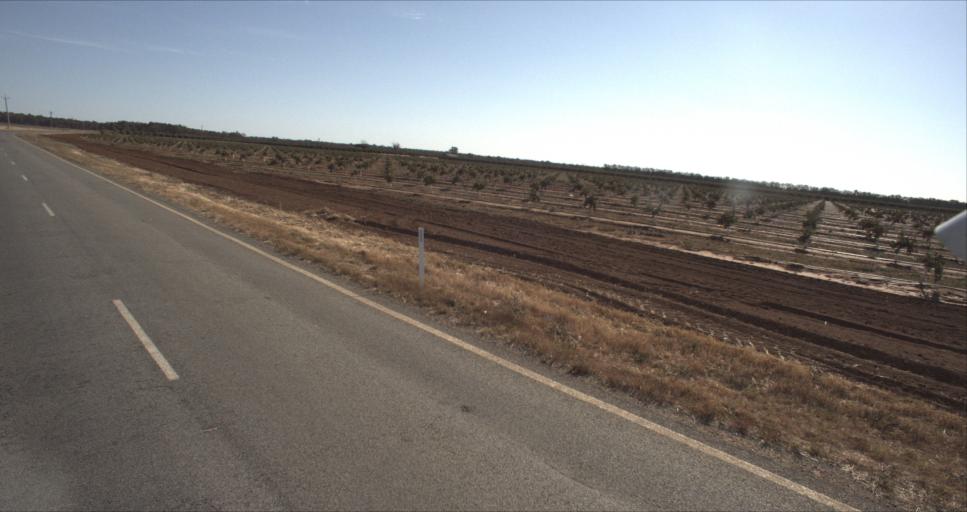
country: AU
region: New South Wales
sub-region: Leeton
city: Leeton
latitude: -34.6120
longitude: 146.4035
